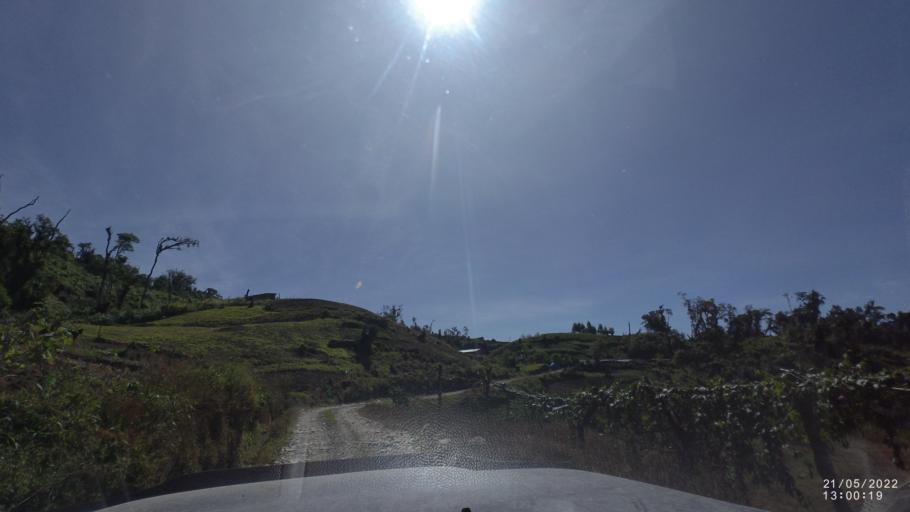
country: BO
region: Cochabamba
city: Colomi
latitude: -17.1638
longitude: -65.9508
